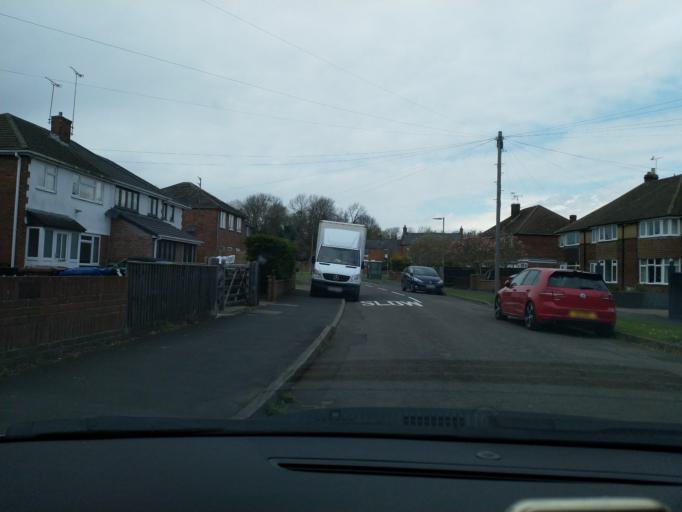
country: GB
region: England
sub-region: Suffolk
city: Woodbridge
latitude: 52.0697
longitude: 1.3250
